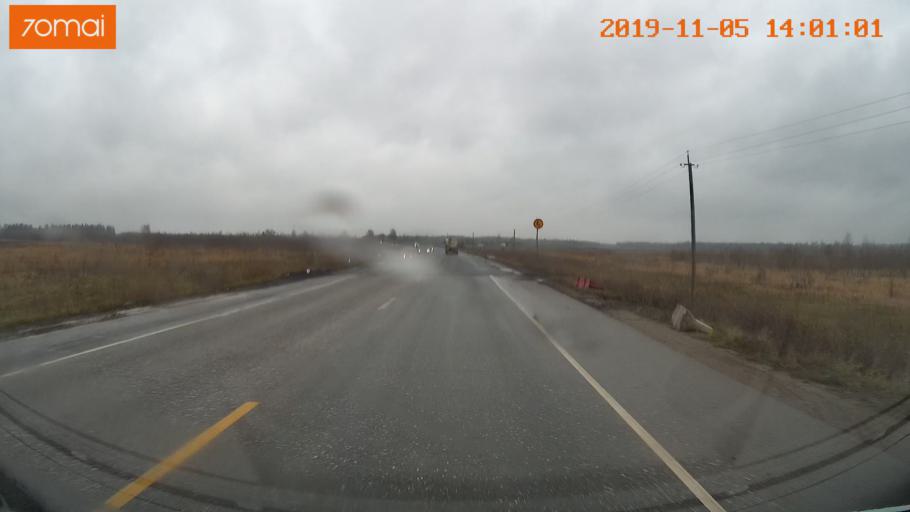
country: RU
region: Ivanovo
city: Kitovo
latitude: 57.0115
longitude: 41.2376
